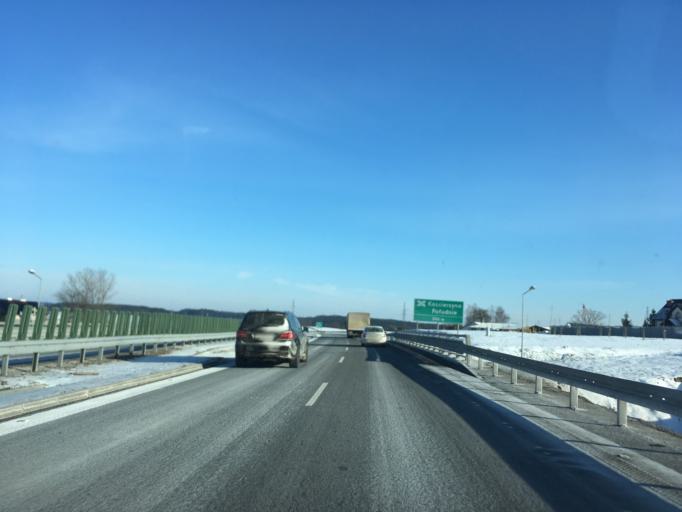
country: PL
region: Pomeranian Voivodeship
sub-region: Powiat koscierski
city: Koscierzyna
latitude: 54.1081
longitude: 17.9617
